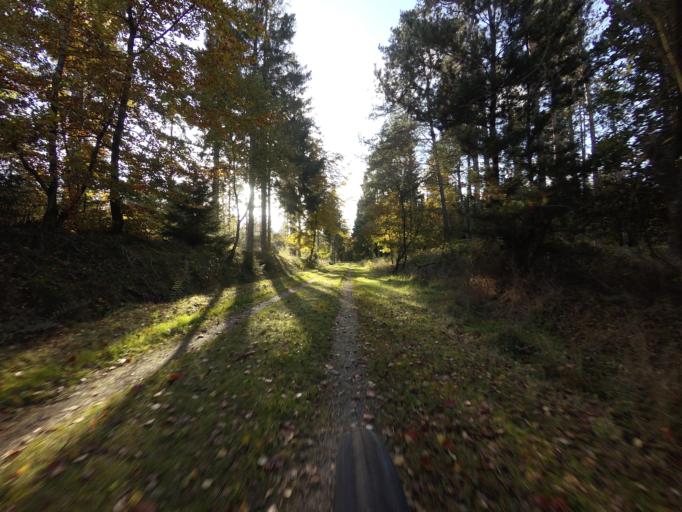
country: DK
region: Central Jutland
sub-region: Norddjurs Kommune
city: Grenaa
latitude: 56.4930
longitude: 10.6932
